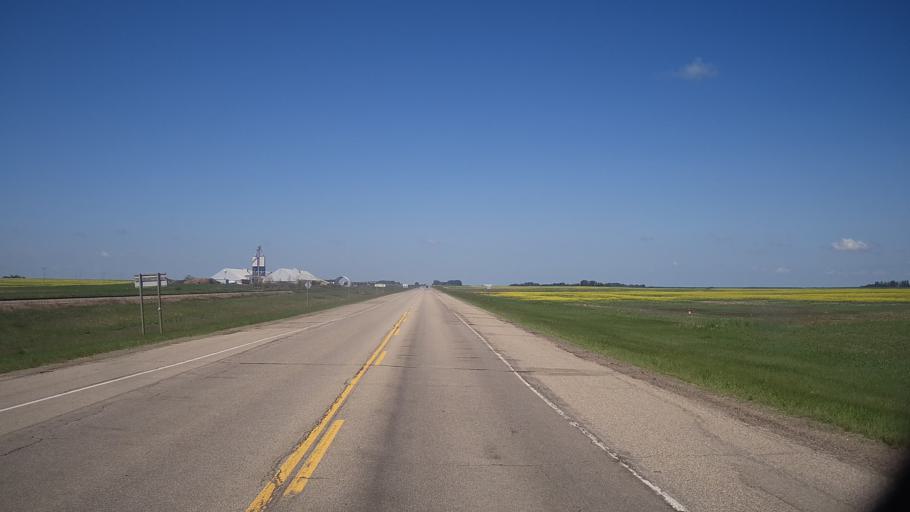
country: CA
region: Saskatchewan
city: Saskatoon
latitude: 51.9916
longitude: -106.0777
